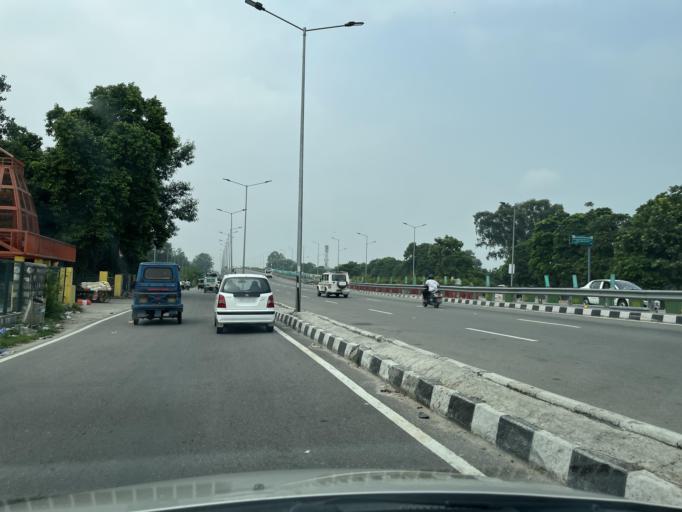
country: IN
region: Uttarakhand
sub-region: Haridwar
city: Haridwar
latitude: 29.9491
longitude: 78.1683
